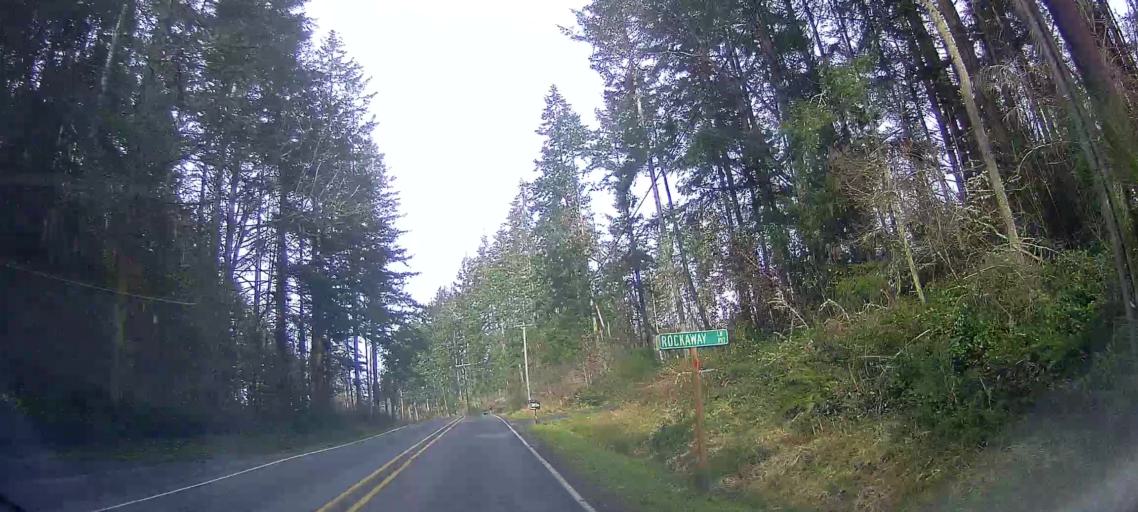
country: US
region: Washington
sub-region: Island County
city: Camano
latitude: 48.2047
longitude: -122.5323
